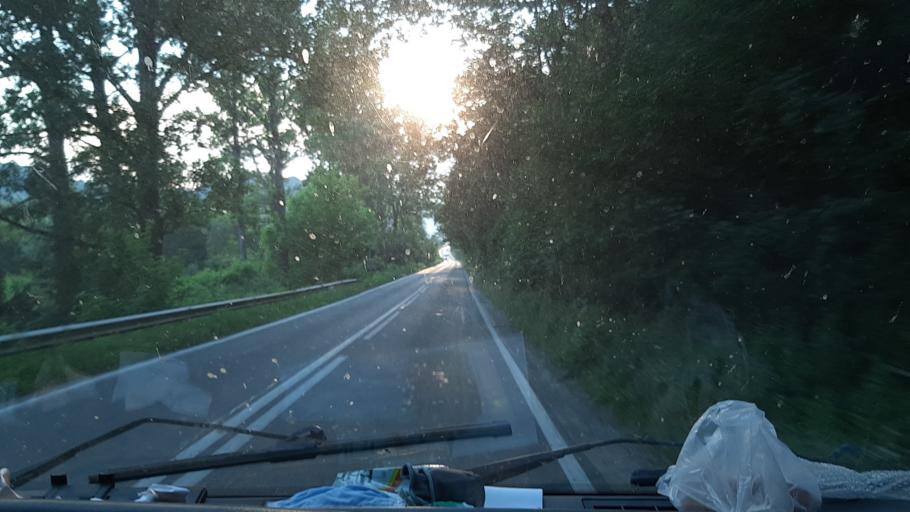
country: RO
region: Caras-Severin
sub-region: Municipiul Resita
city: Calnic
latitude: 45.3674
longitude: 21.8069
